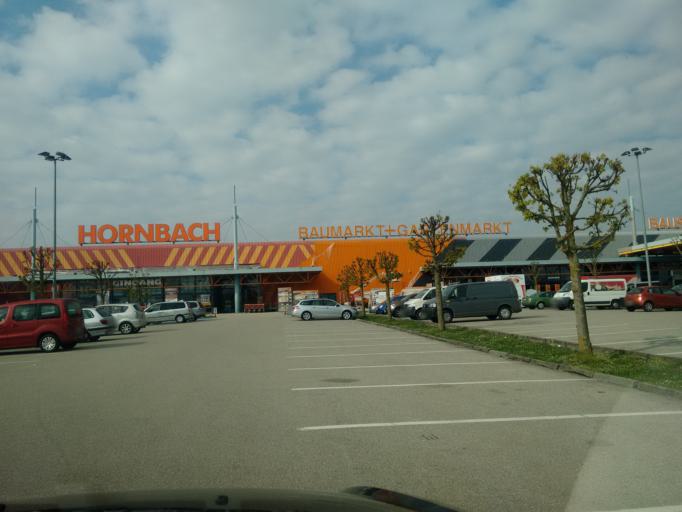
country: AT
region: Upper Austria
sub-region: Wels-Land
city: Gunskirchen
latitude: 48.1490
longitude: 13.9742
